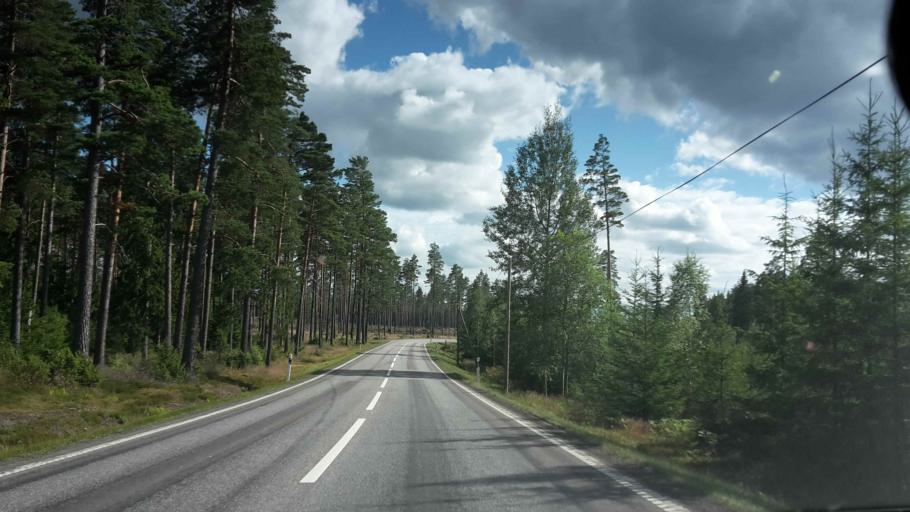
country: SE
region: OErebro
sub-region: Hallsbergs Kommun
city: Palsboda
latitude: 58.8587
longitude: 15.4081
